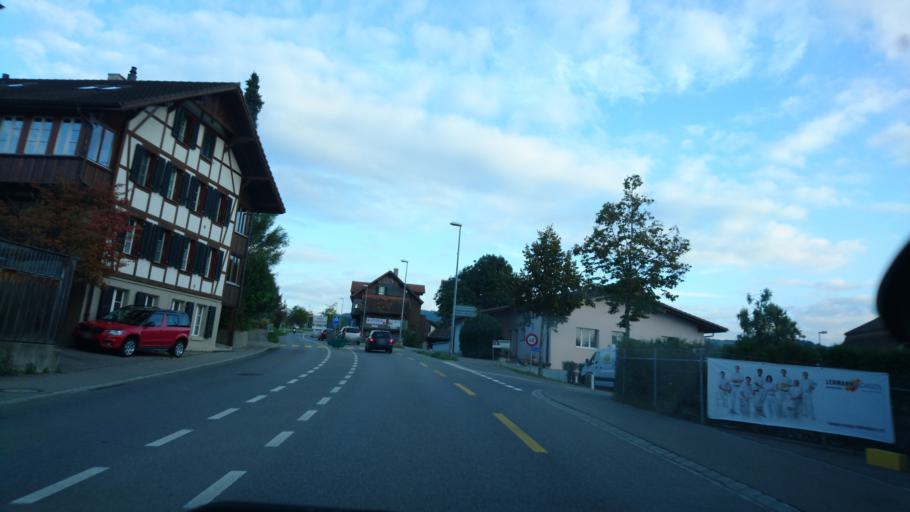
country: CH
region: Bern
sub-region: Bern-Mittelland District
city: Worb
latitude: 46.9183
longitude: 7.5834
